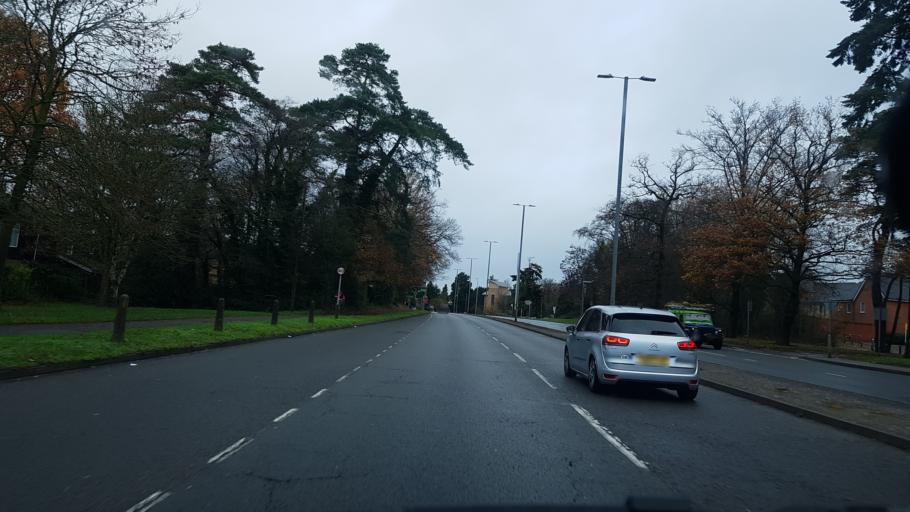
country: GB
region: England
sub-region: Bracknell Forest
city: Bracknell
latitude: 51.4058
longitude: -0.7475
